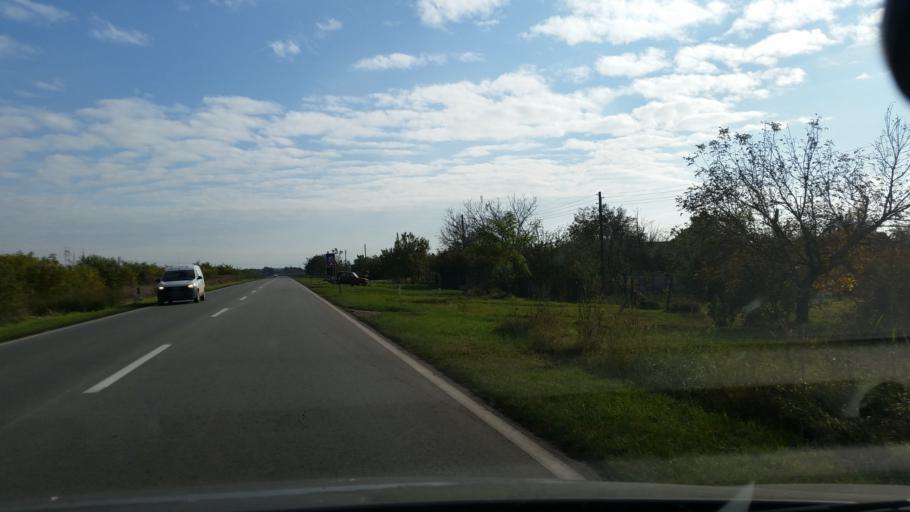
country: RS
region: Autonomna Pokrajina Vojvodina
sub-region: Srednjebanatski Okrug
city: Zrenjanin
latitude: 45.4170
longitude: 20.3720
